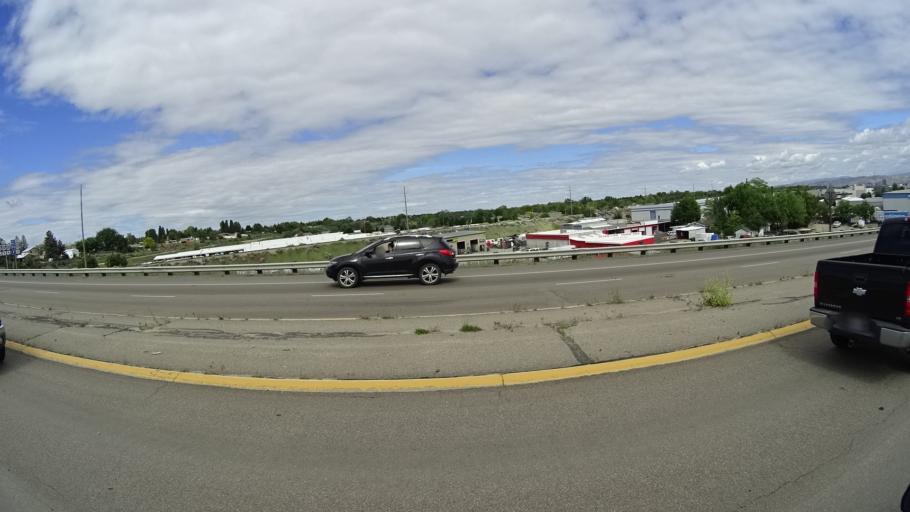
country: US
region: Idaho
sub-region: Ada County
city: Boise
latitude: 43.5700
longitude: -116.1939
